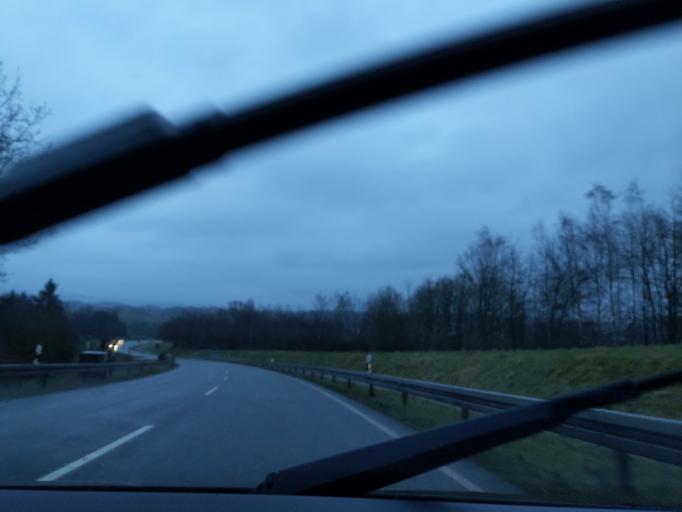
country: DE
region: Hesse
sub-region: Regierungsbezirk Kassel
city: Bad Arolsen
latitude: 51.3805
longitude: 9.0426
